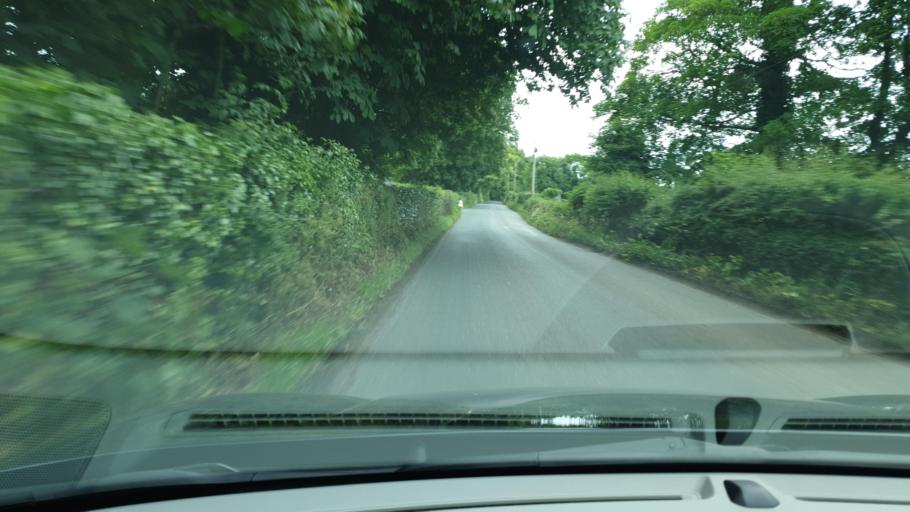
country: IE
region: Leinster
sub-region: An Mhi
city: Dunboyne
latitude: 53.4095
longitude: -6.4725
